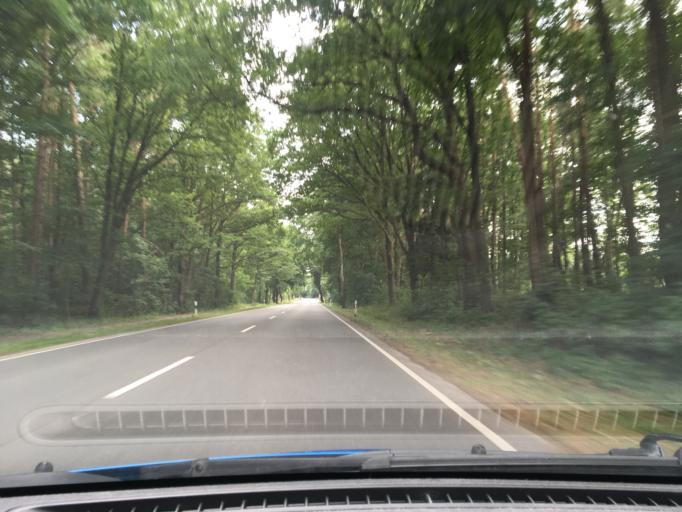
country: DE
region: Lower Saxony
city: Kakenstorf
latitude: 53.2954
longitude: 9.7952
